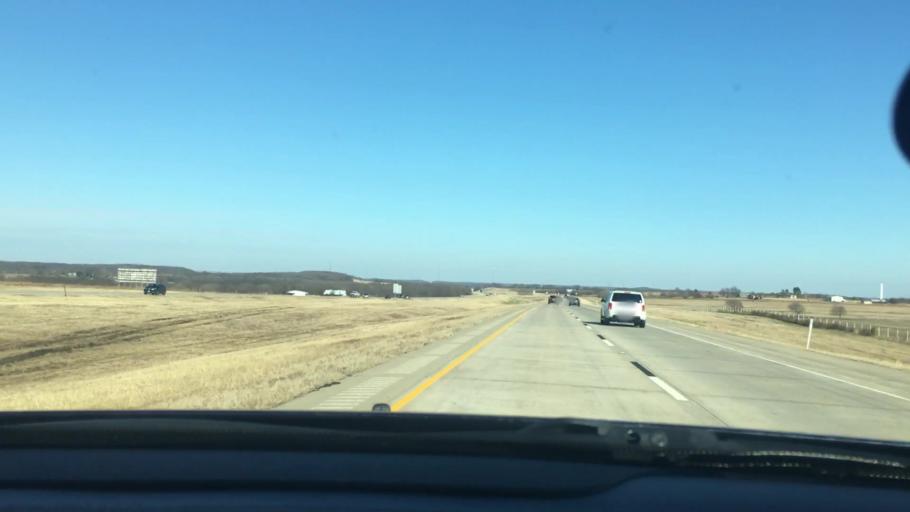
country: US
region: Oklahoma
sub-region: Love County
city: Marietta
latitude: 33.9673
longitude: -97.1340
